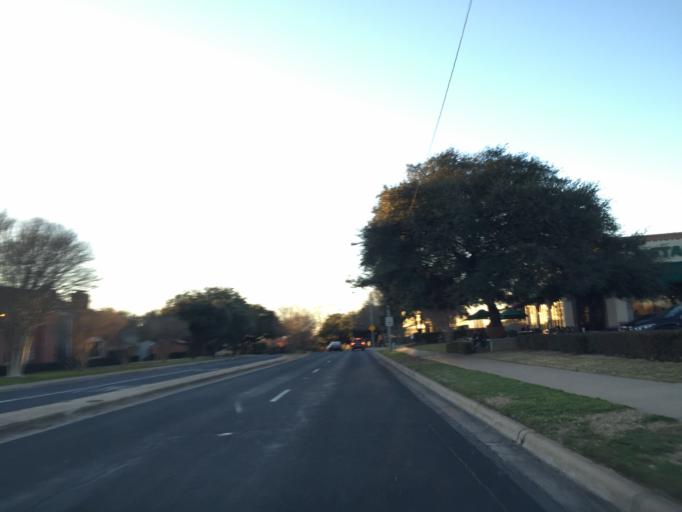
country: US
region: Texas
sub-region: Williamson County
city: Jollyville
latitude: 30.3946
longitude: -97.7522
